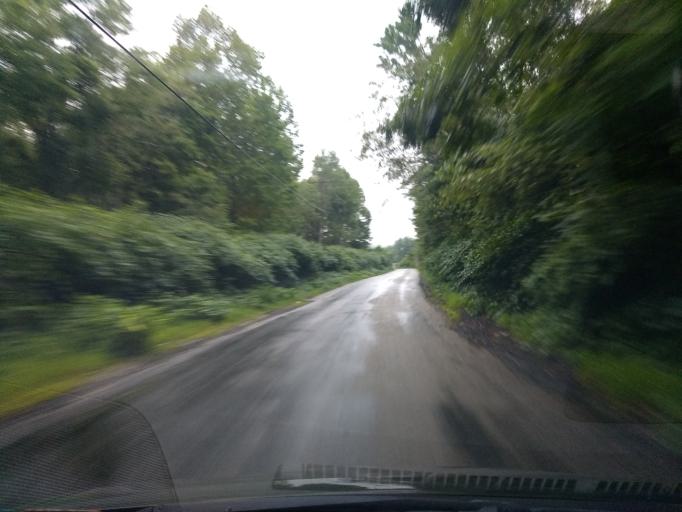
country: US
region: Pennsylvania
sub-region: Westmoreland County
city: Greensburg
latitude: 40.3500
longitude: -79.5171
